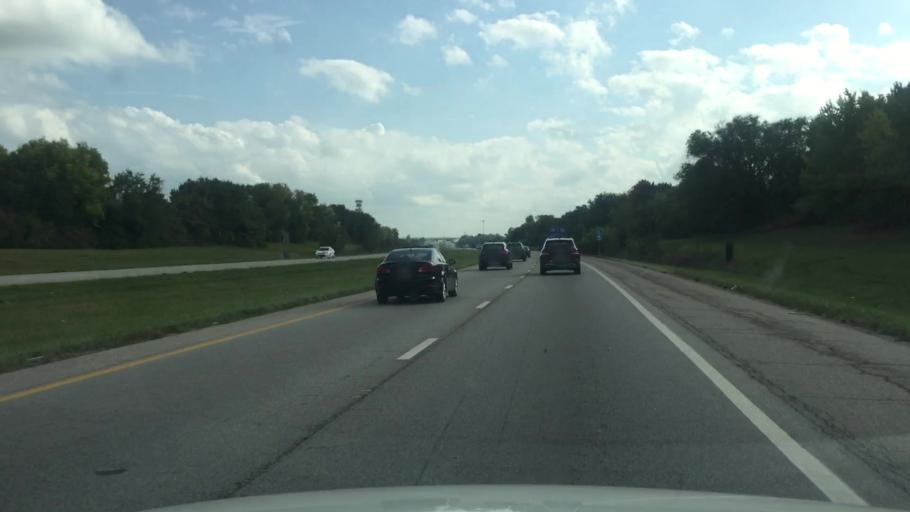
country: US
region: Kansas
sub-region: Johnson County
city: Lenexa
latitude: 38.8629
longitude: -94.6778
